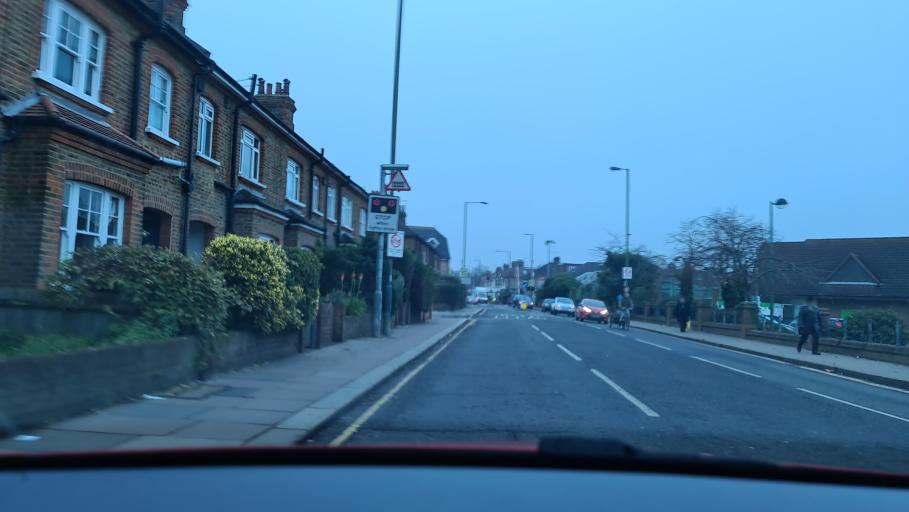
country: GB
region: England
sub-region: Greater London
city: Richmond
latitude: 51.4661
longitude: -0.2885
